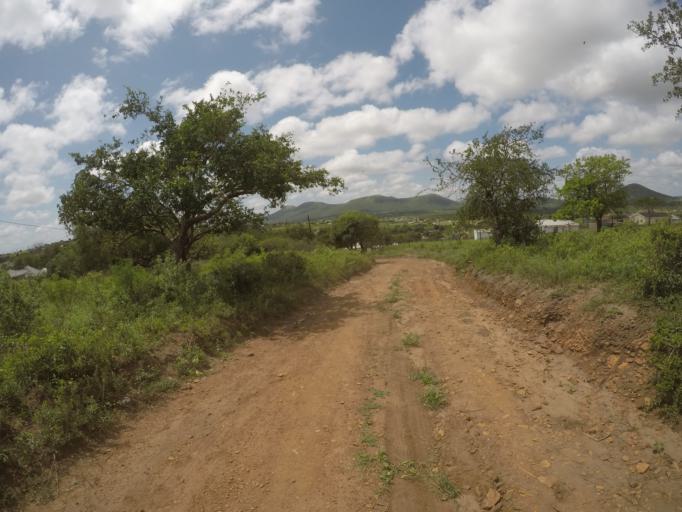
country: ZA
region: KwaZulu-Natal
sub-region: uThungulu District Municipality
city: Empangeni
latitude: -28.5844
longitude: 31.8371
